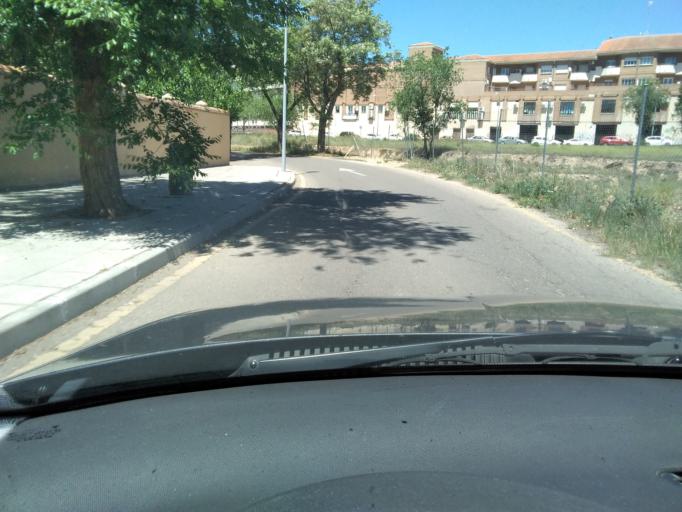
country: ES
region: Castille-La Mancha
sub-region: Province of Toledo
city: Toledo
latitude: 39.8711
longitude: -4.0405
